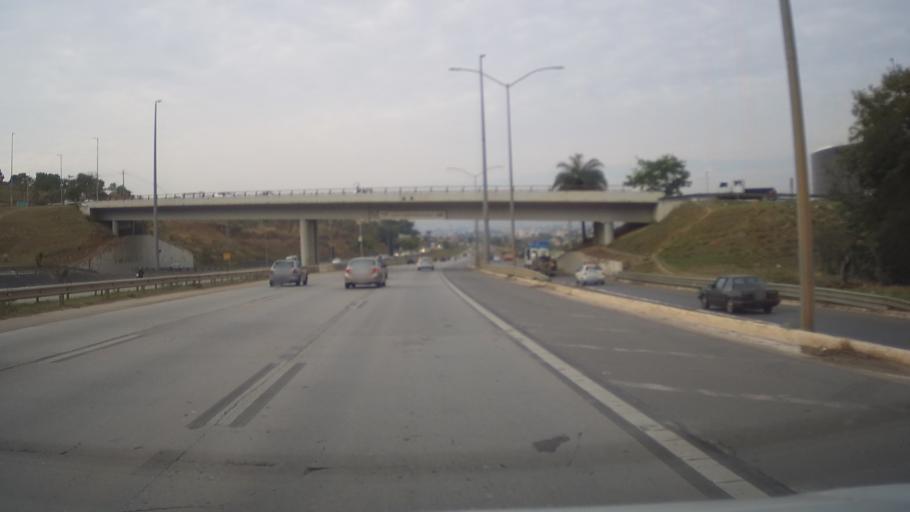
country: BR
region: Minas Gerais
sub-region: Vespasiano
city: Vespasiano
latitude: -19.7789
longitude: -43.9488
